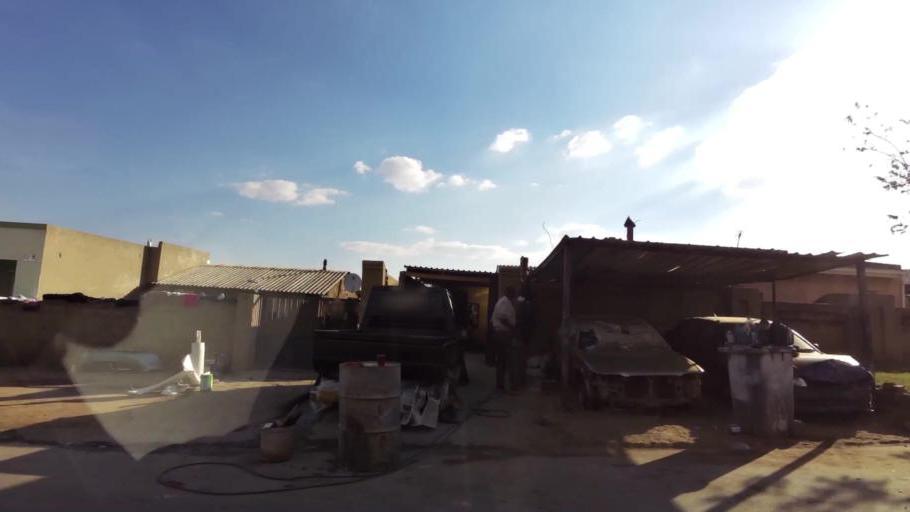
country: ZA
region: Gauteng
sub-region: City of Johannesburg Metropolitan Municipality
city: Roodepoort
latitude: -26.2047
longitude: 27.8838
